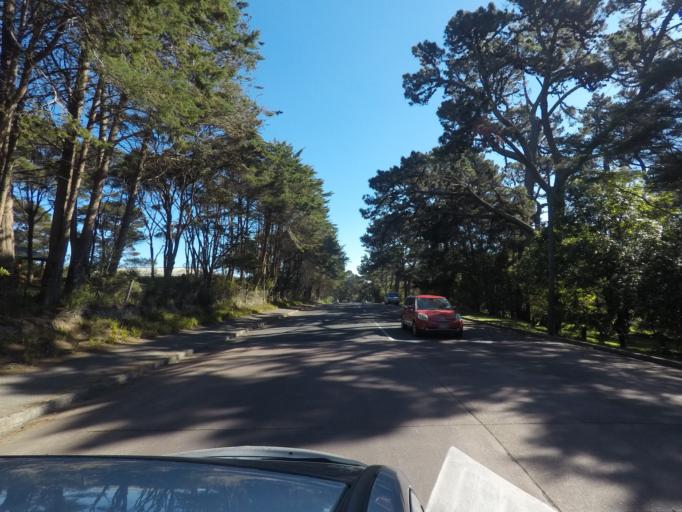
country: NZ
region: Auckland
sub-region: Auckland
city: Waitakere
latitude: -36.9290
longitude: 174.6915
